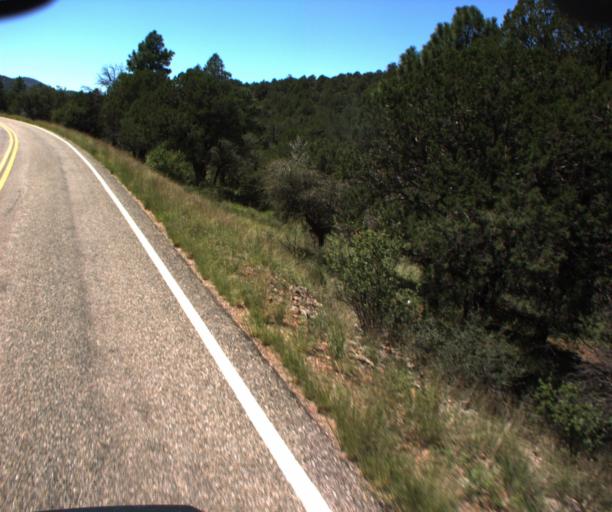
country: US
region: Arizona
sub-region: Greenlee County
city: Morenci
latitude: 33.2810
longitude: -109.3559
